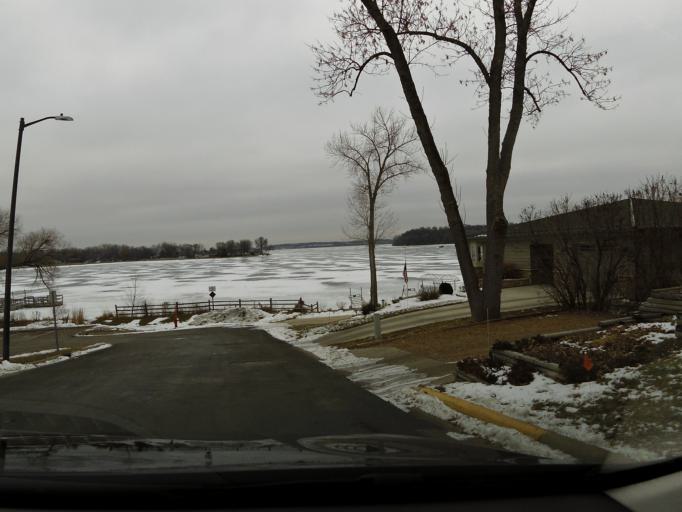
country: US
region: Minnesota
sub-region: Carver County
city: Waconia
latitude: 44.8521
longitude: -93.7922
